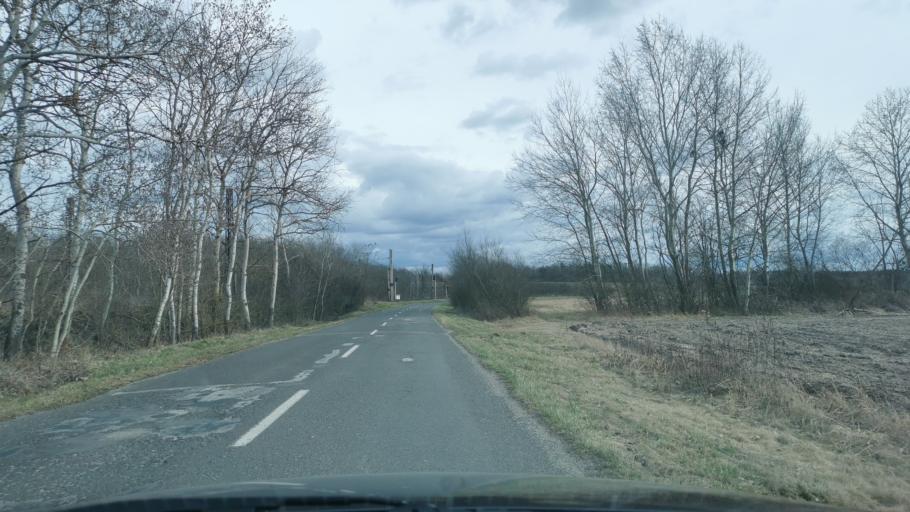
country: CZ
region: South Moravian
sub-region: Okres Breclav
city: Lanzhot
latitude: 48.6869
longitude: 17.0280
